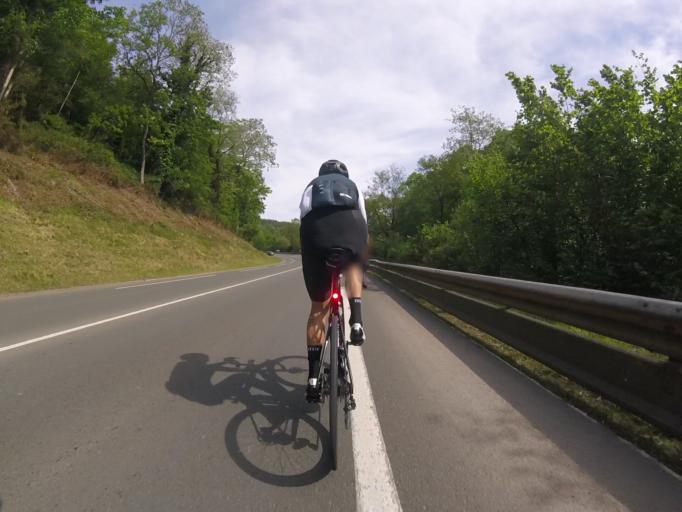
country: ES
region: Basque Country
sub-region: Provincia de Guipuzcoa
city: Cestona
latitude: 43.2535
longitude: -2.2617
